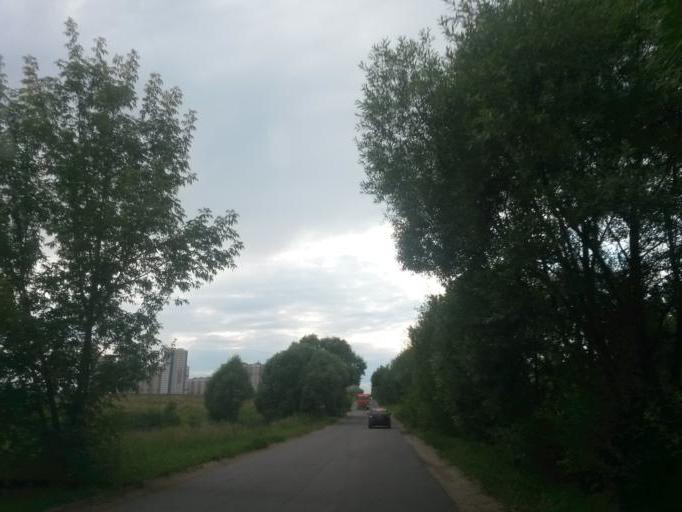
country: RU
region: Moskovskaya
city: Vostryakovo
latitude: 55.3954
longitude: 37.7864
